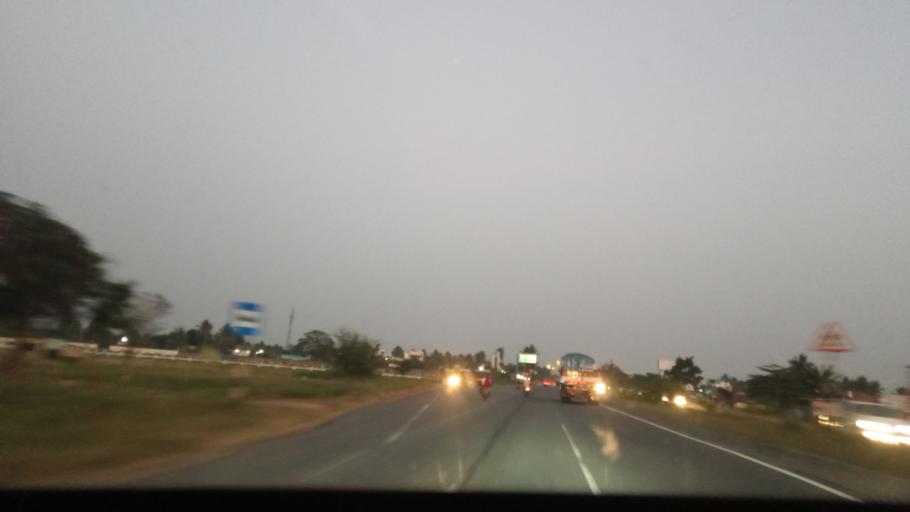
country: IN
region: Tamil Nadu
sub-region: Salem
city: Attur
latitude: 11.6174
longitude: 78.5575
